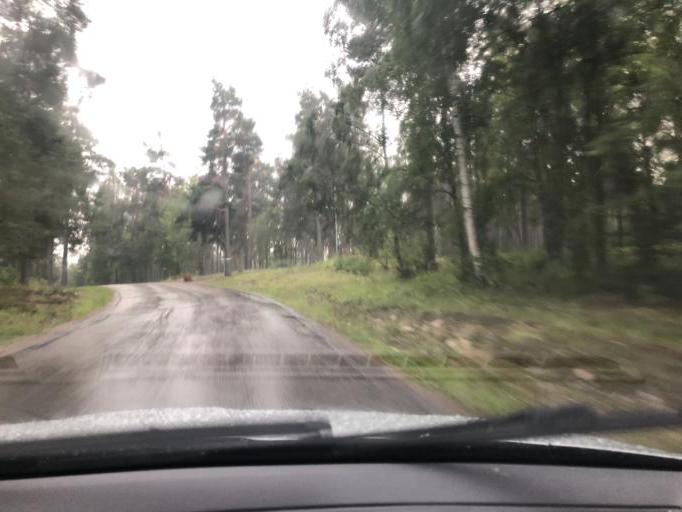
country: SE
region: Vaesternorrland
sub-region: Sundsvalls Kommun
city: Sundsvall
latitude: 62.4023
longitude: 17.3077
